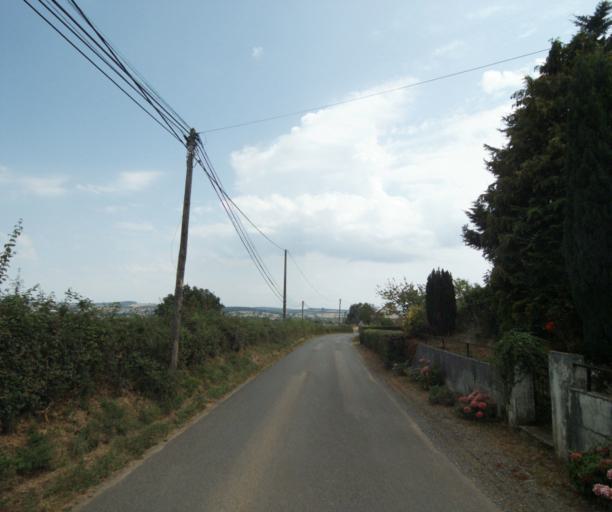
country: FR
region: Bourgogne
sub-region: Departement de Saone-et-Loire
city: Gueugnon
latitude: 46.5982
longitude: 4.0314
